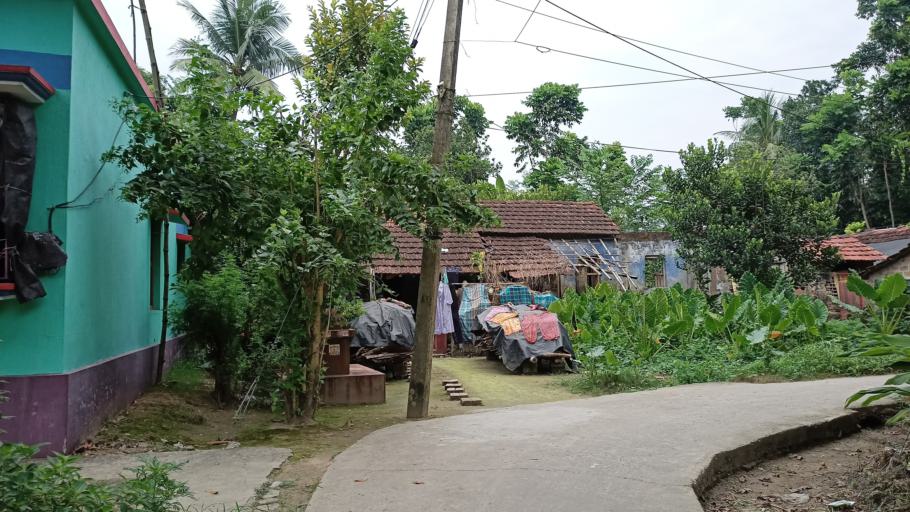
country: IN
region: West Bengal
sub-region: North 24 Parganas
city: Bangaon
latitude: 23.0655
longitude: 88.8198
